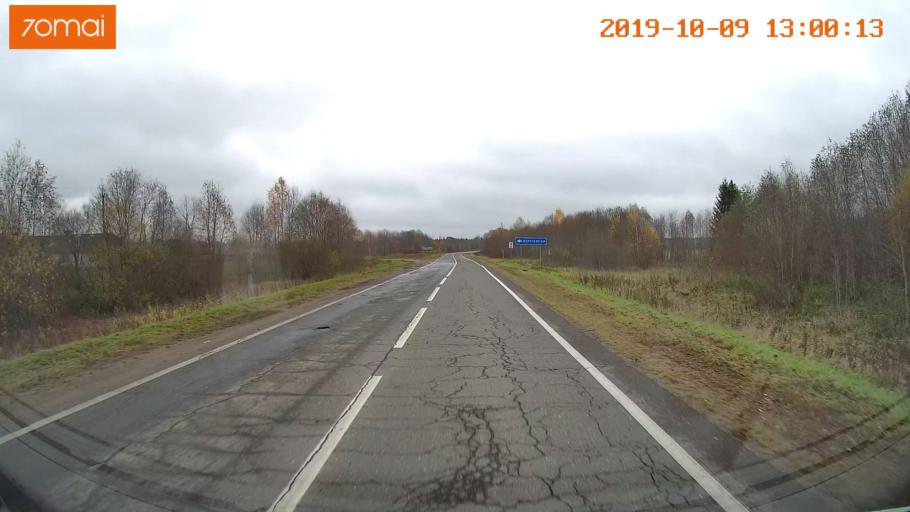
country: RU
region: Jaroslavl
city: Prechistoye
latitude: 58.3791
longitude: 40.4771
